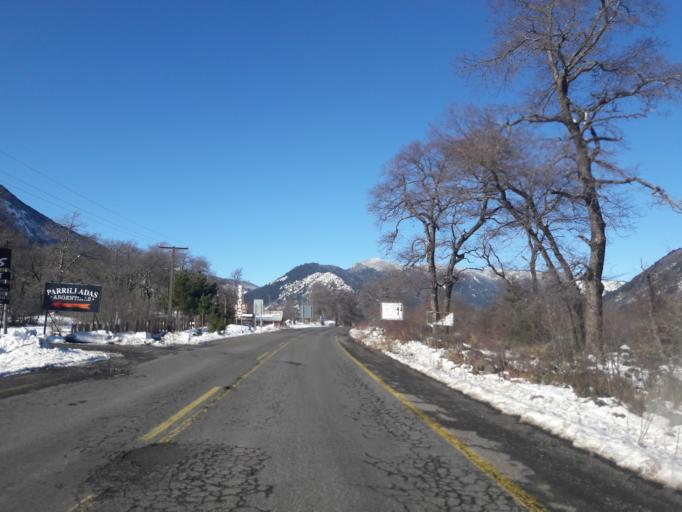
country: CL
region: Araucania
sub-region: Provincia de Cautin
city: Vilcun
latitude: -38.4723
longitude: -71.5630
